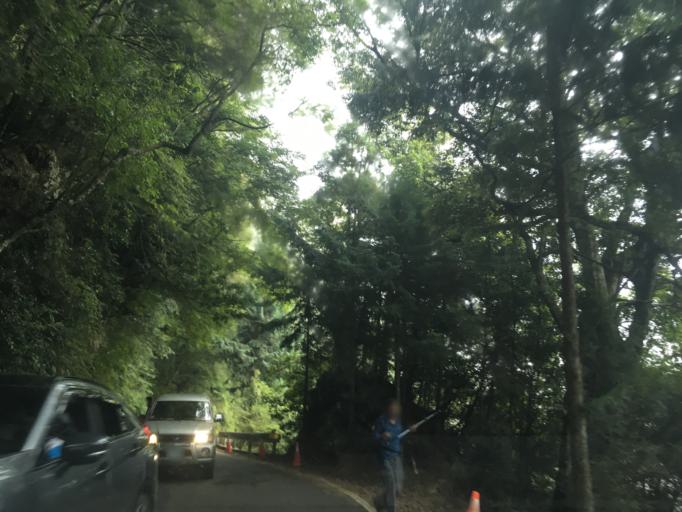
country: TW
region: Taiwan
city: Fengyuan
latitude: 24.2350
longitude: 120.9580
